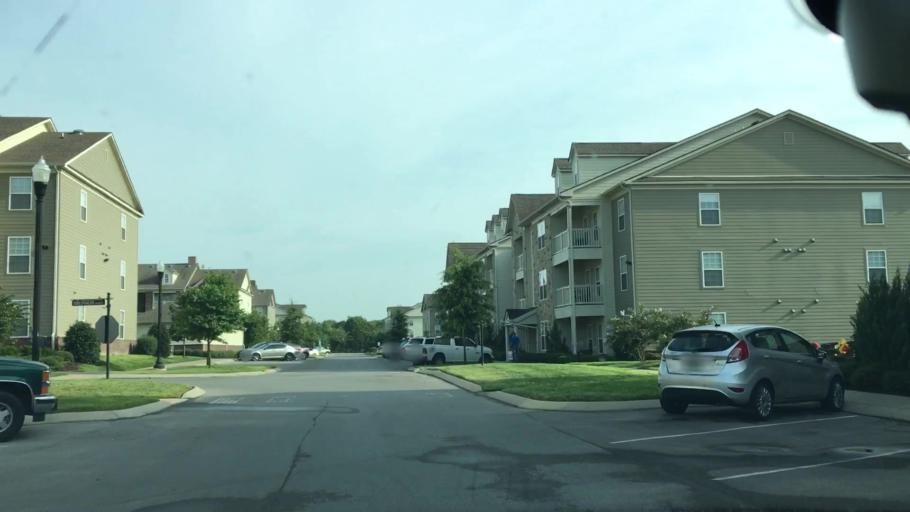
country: US
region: Tennessee
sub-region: Wilson County
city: Lebanon
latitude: 36.2314
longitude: -86.3651
